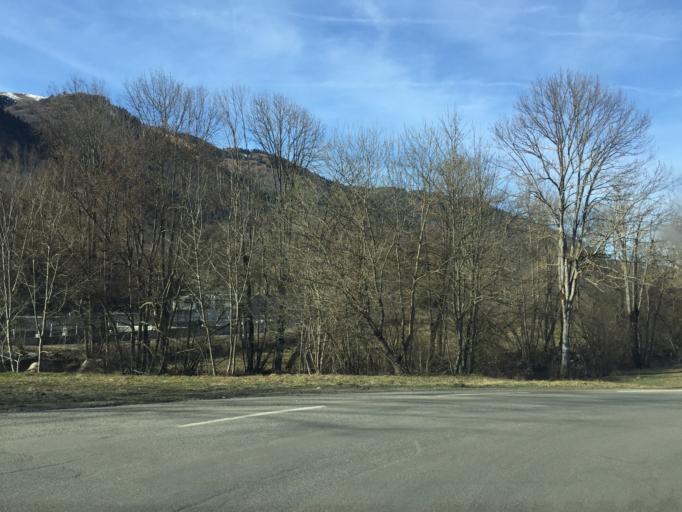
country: FR
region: Midi-Pyrenees
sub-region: Departement des Hautes-Pyrenees
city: Saint-Lary-Soulan
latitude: 42.8120
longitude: 0.4091
